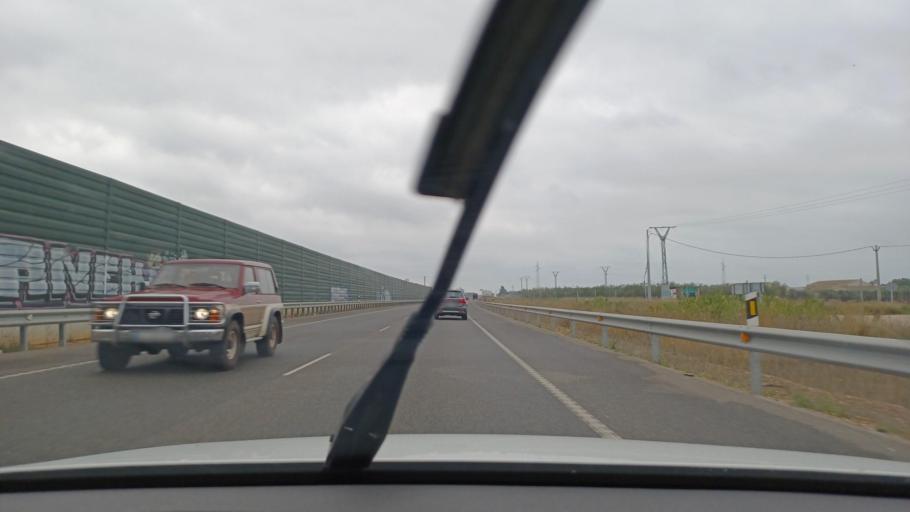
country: ES
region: Valencia
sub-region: Provincia de Castello
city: Benicarlo
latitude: 40.4237
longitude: 0.3929
